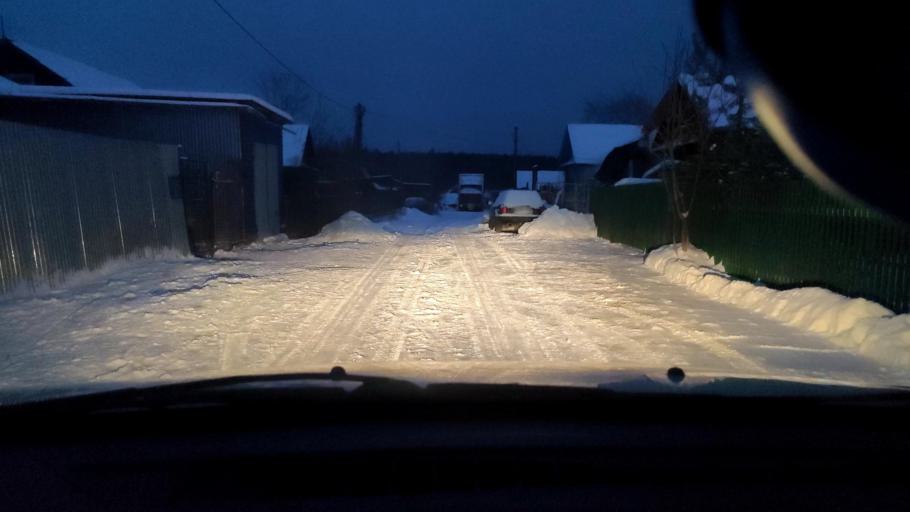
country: RU
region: Perm
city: Kondratovo
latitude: 58.0490
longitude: 56.0538
